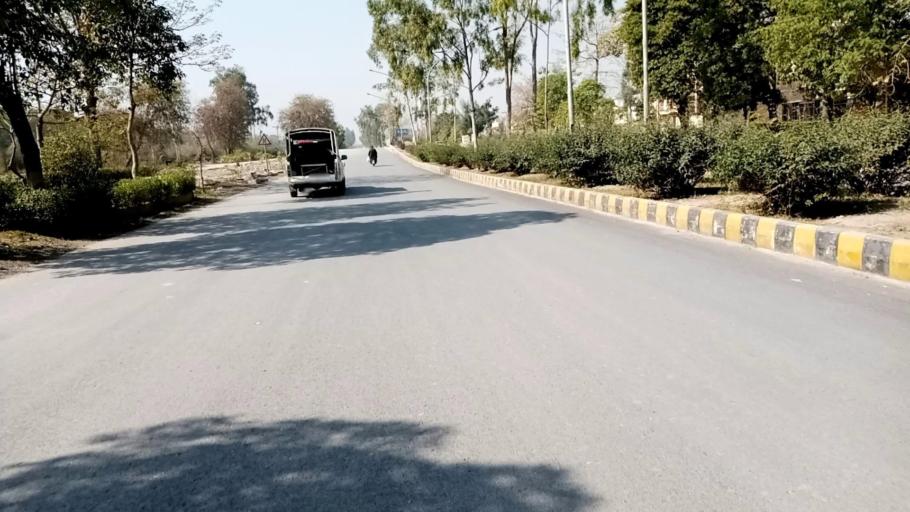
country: PK
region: Khyber Pakhtunkhwa
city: Peshawar
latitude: 33.9564
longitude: 71.4258
